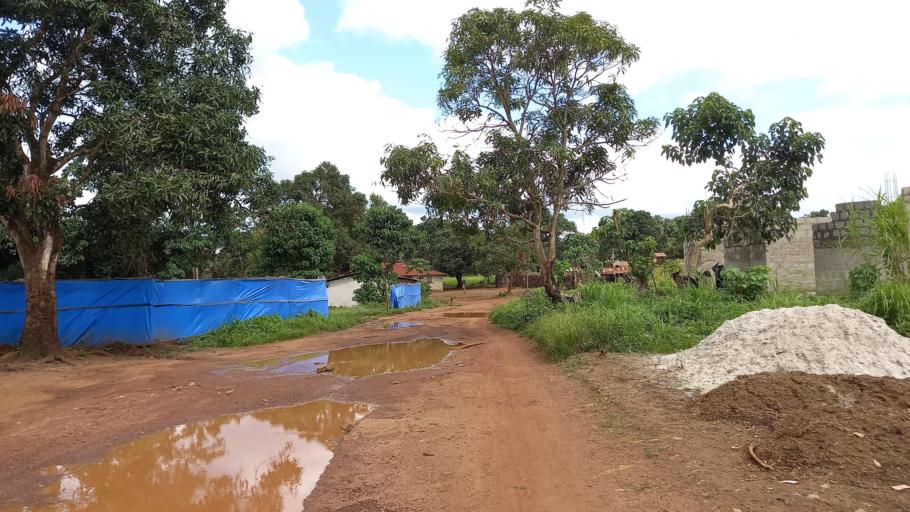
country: SL
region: Northern Province
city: Kamakwie
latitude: 9.5022
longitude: -12.2375
